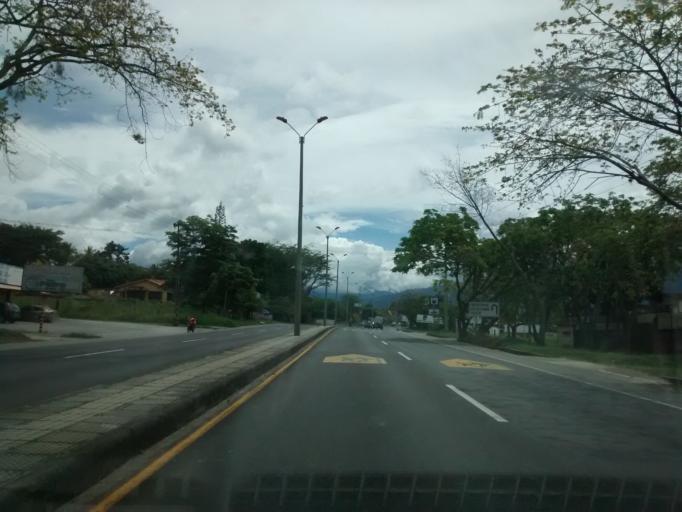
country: CO
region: Tolima
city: Ibague
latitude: 4.4054
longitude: -75.1635
